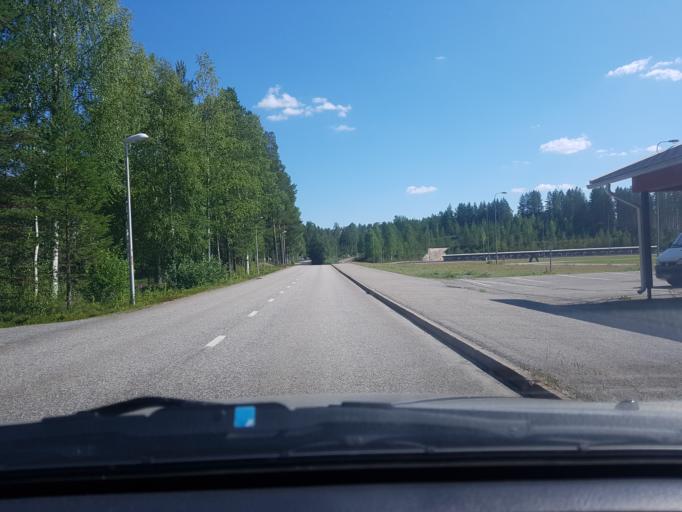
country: FI
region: Kainuu
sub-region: Kehys-Kainuu
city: Kuhmo
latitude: 64.1196
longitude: 29.5832
